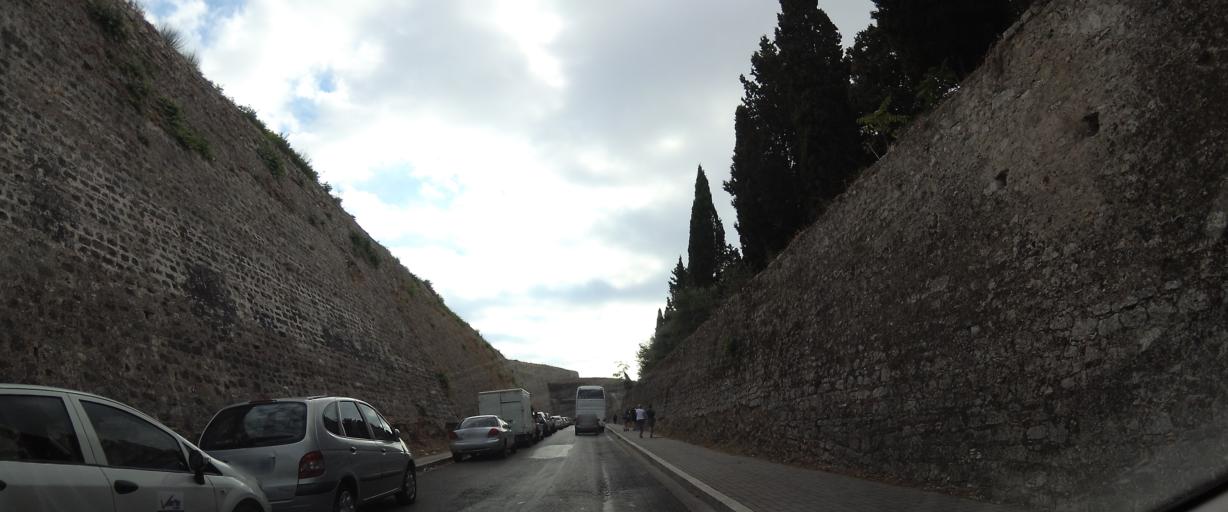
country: GR
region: Ionian Islands
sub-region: Nomos Kerkyras
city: Kerkyra
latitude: 39.6259
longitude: 19.9145
